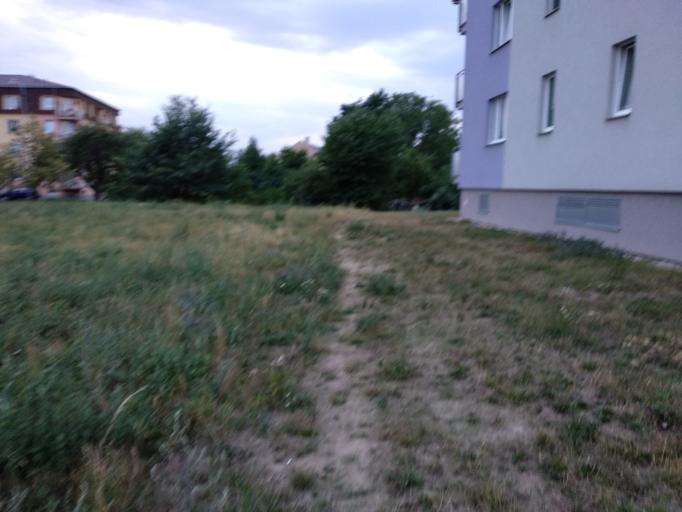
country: CZ
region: Olomoucky
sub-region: Okres Olomouc
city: Olomouc
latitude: 49.5712
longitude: 17.2517
